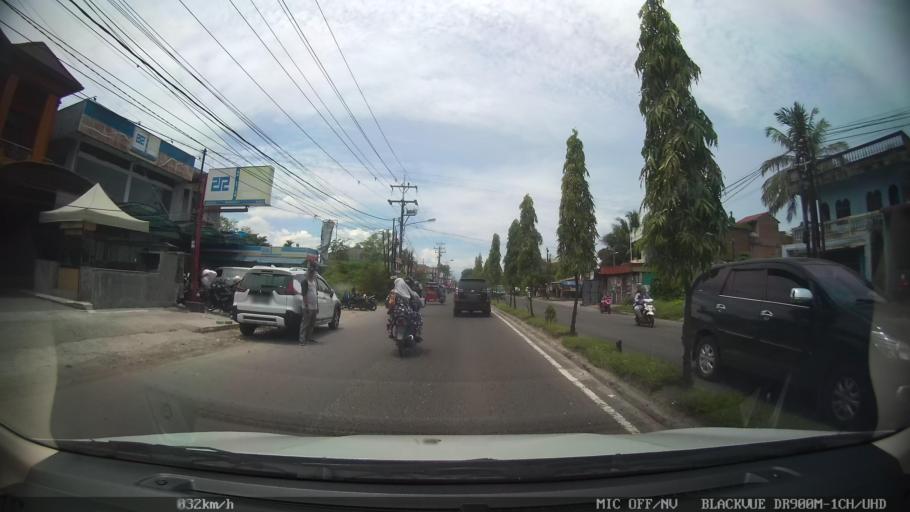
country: ID
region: North Sumatra
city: Sunggal
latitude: 3.5399
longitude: 98.6224
